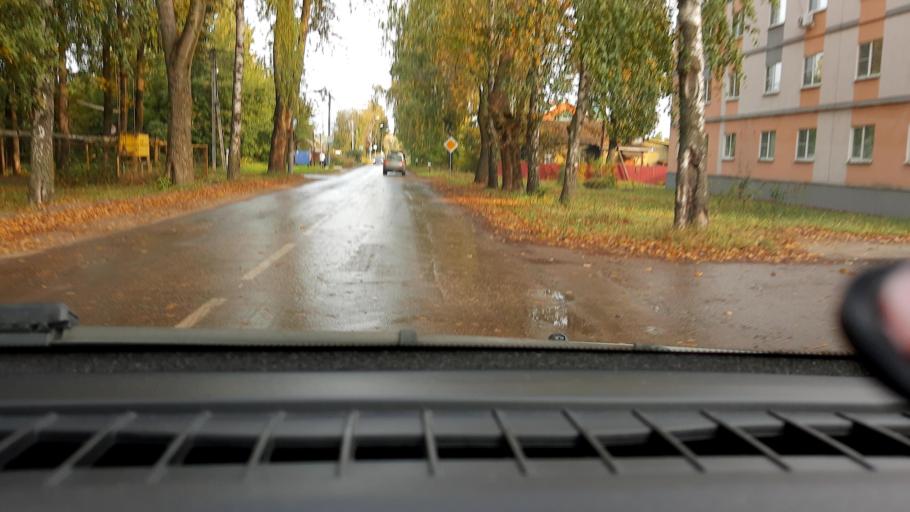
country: RU
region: Nizjnij Novgorod
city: Kstovo
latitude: 56.1850
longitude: 44.1646
